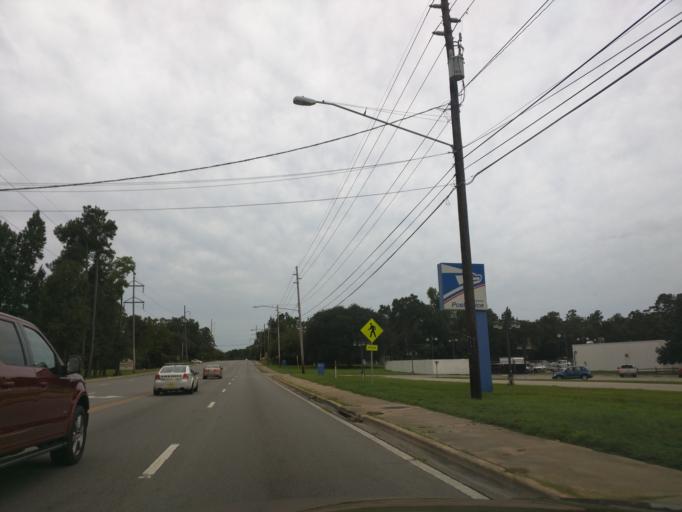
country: US
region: Florida
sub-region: Leon County
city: Tallahassee
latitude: 30.4118
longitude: -84.2832
